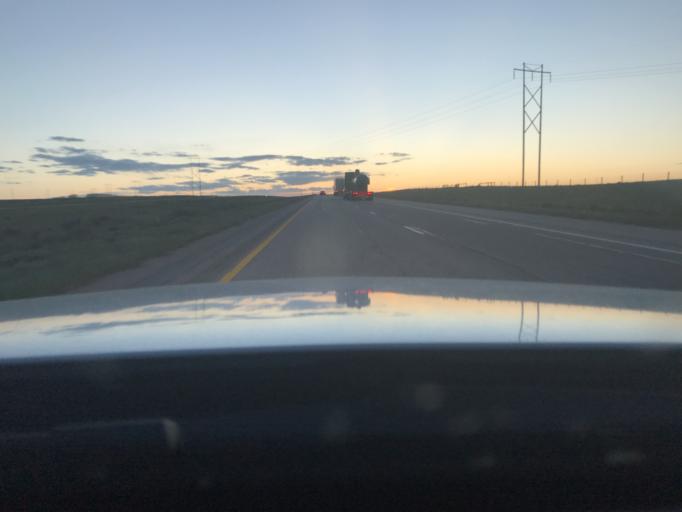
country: US
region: Wyoming
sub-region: Converse County
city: Glenrock
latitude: 42.8294
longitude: -105.8301
